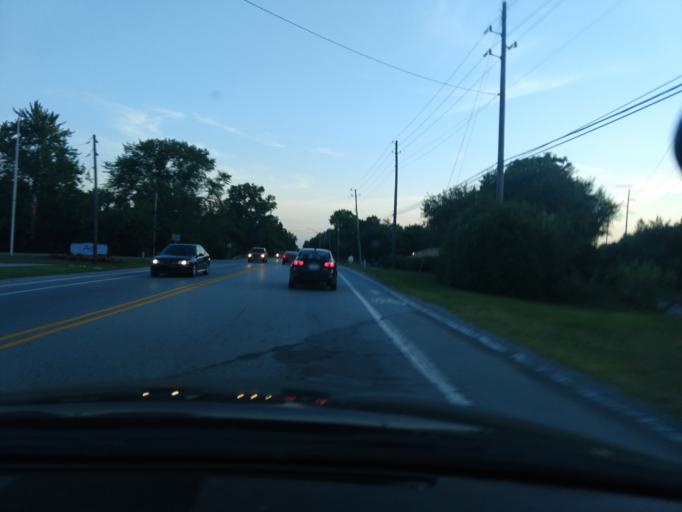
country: US
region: Indiana
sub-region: Marion County
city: Broad Ripple
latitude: 39.8673
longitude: -86.0977
